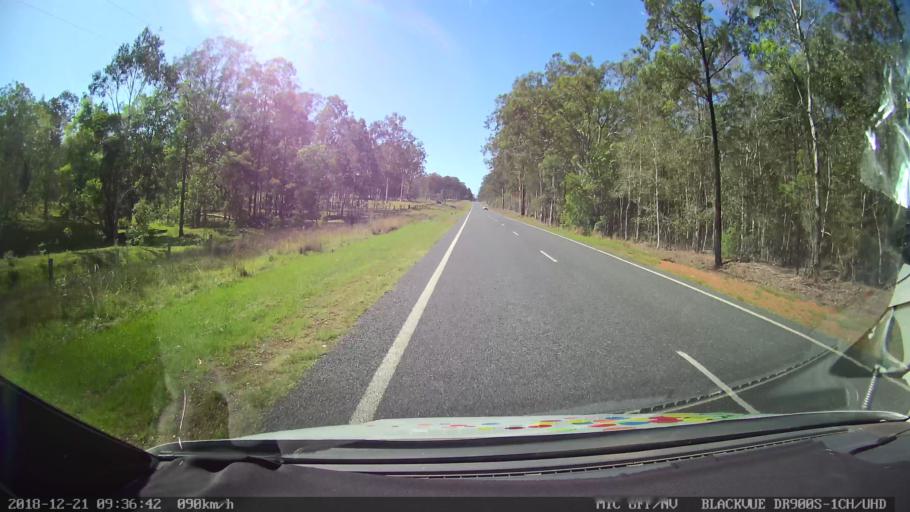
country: AU
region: New South Wales
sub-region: Clarence Valley
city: Grafton
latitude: -29.5268
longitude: 152.9841
